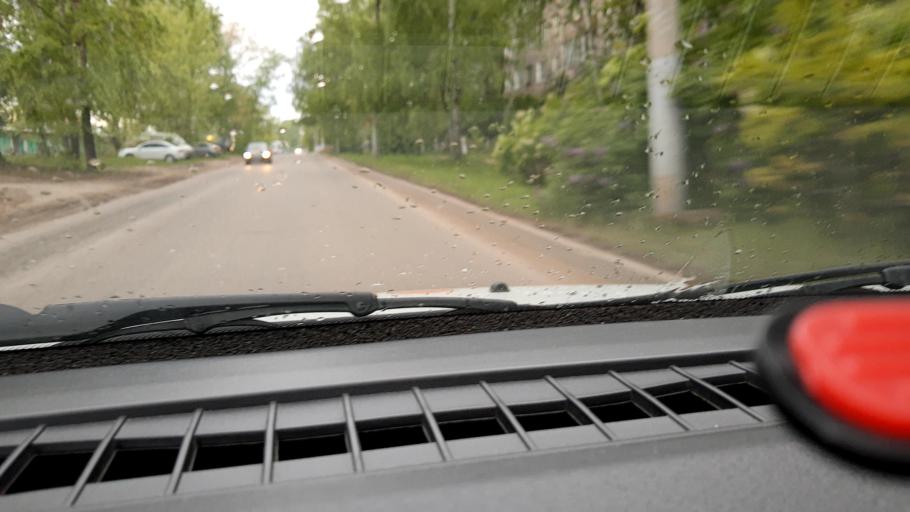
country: RU
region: Nizjnij Novgorod
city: Gorbatovka
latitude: 56.3550
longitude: 43.8162
